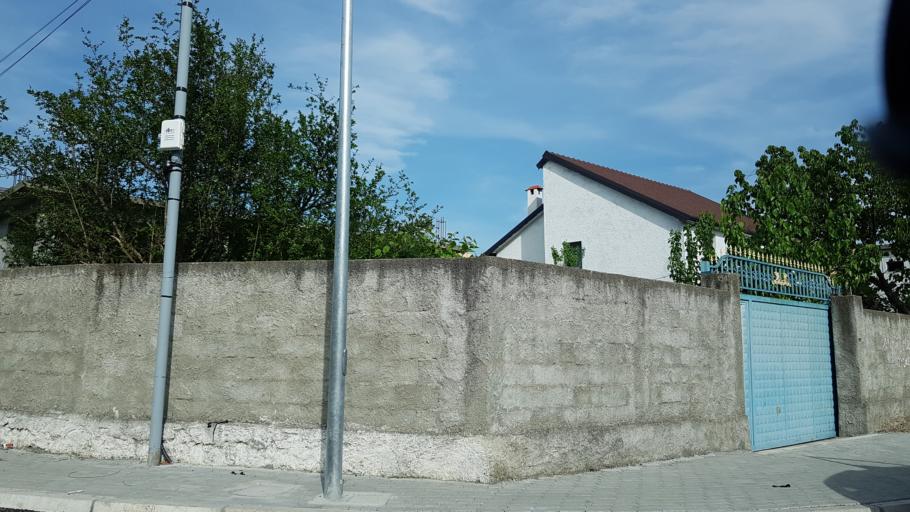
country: AL
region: Shkoder
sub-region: Rrethi i Shkodres
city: Shkoder
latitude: 42.0758
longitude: 19.5219
